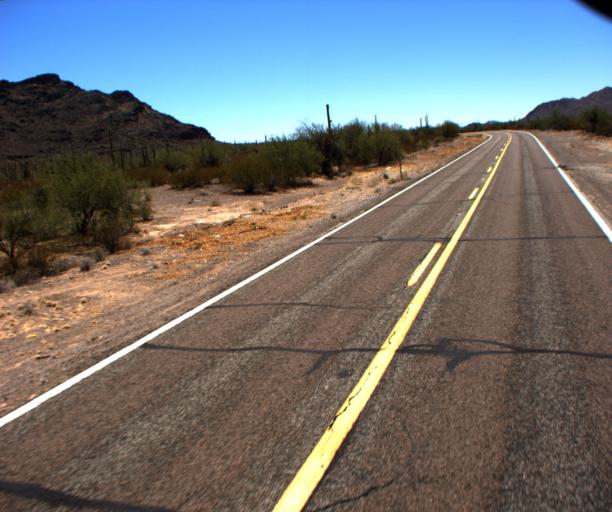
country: US
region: Arizona
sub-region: Pima County
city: Ajo
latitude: 32.2299
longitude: -112.7115
